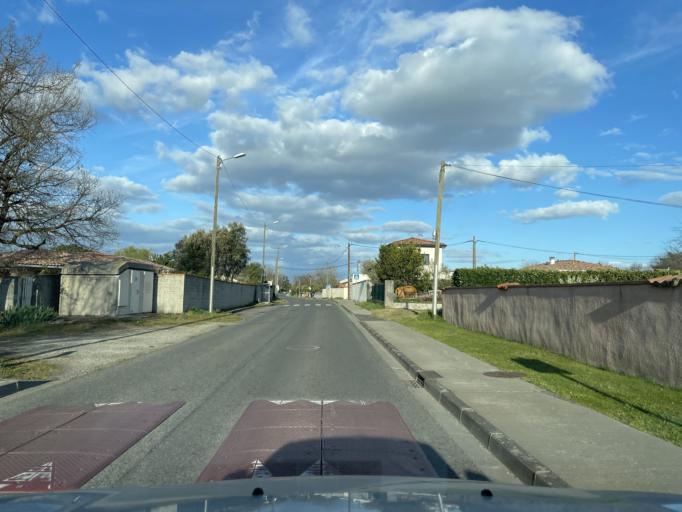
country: FR
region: Midi-Pyrenees
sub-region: Departement de la Haute-Garonne
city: Brax
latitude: 43.6045
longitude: 1.2550
